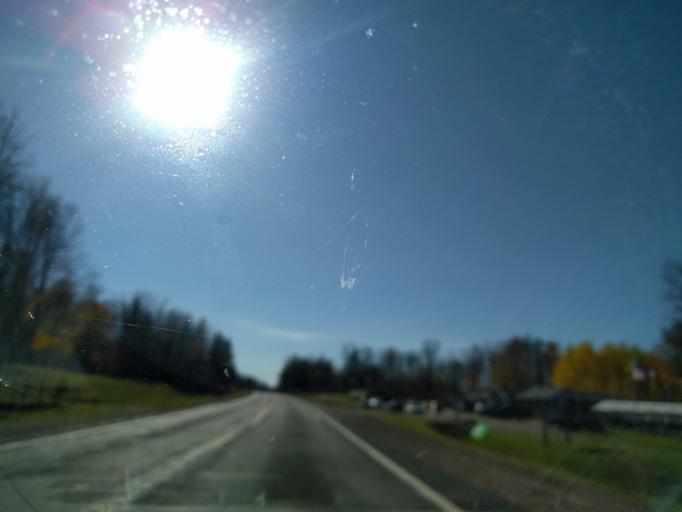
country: US
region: Michigan
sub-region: Iron County
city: Crystal Falls
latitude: 46.1997
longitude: -88.0184
